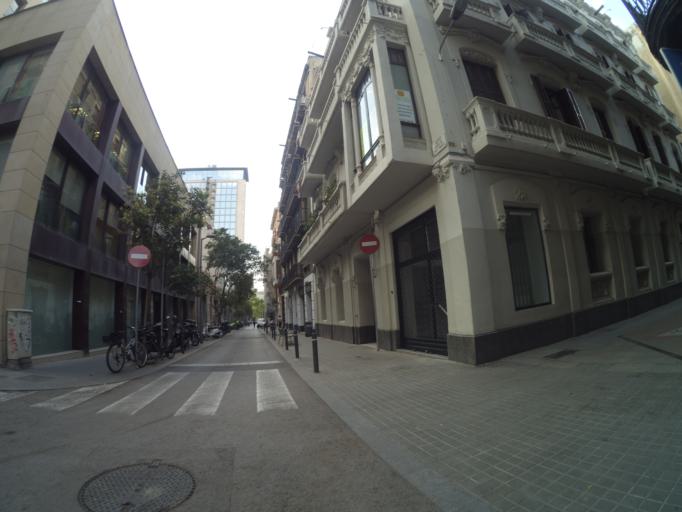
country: ES
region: Catalonia
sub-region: Provincia de Barcelona
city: Gracia
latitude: 41.3975
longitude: 2.1571
